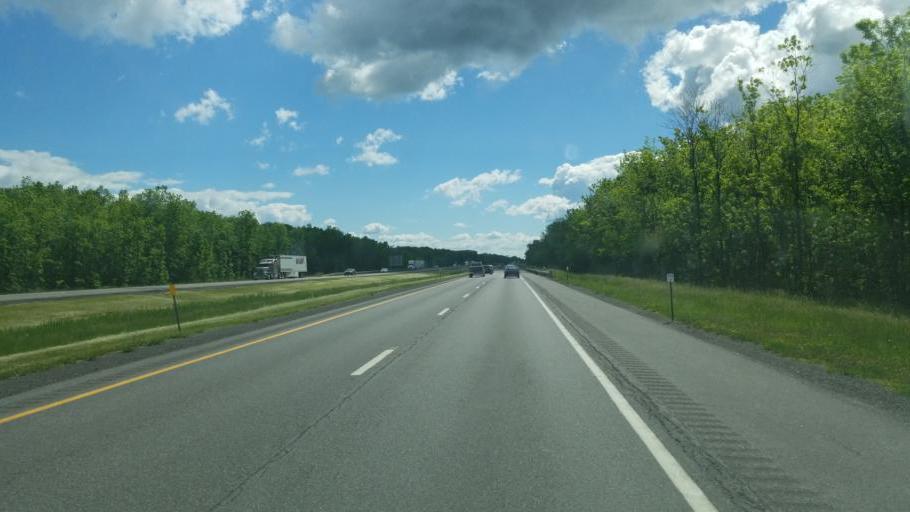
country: US
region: New York
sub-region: Madison County
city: Canastota
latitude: 43.0938
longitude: -75.8134
